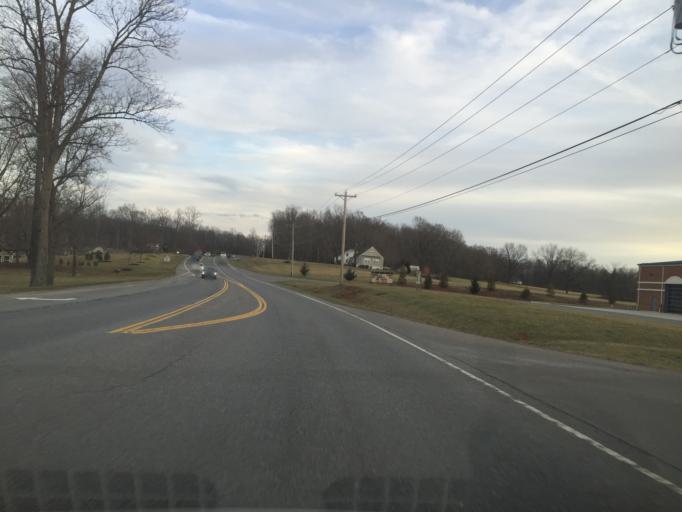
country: US
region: Virginia
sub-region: Bedford County
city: Forest
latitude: 37.3571
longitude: -79.2834
